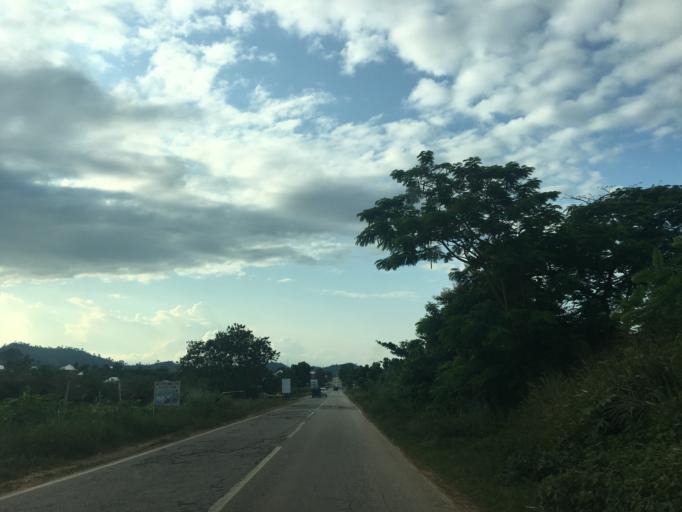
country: GH
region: Western
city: Bibiani
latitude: 6.4225
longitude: -2.3045
